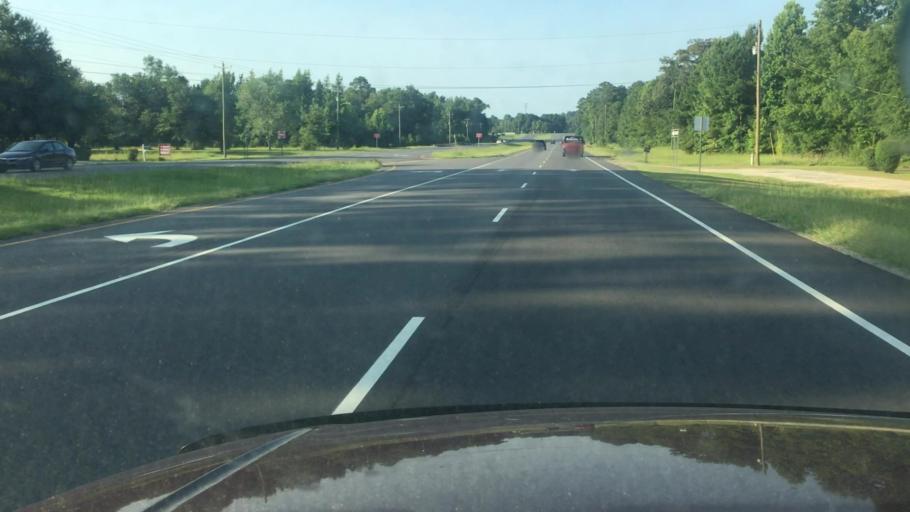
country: US
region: North Carolina
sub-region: Cumberland County
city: Hope Mills
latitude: 34.9440
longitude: -78.8473
